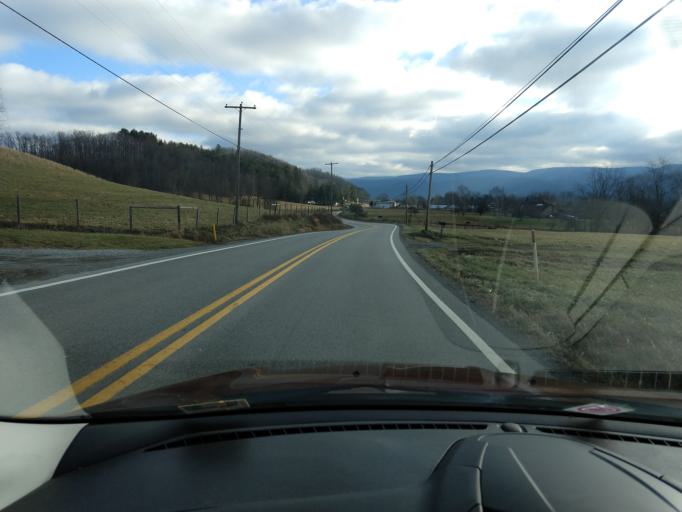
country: US
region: West Virginia
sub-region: Randolph County
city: Elkins
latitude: 38.7714
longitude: -79.9381
